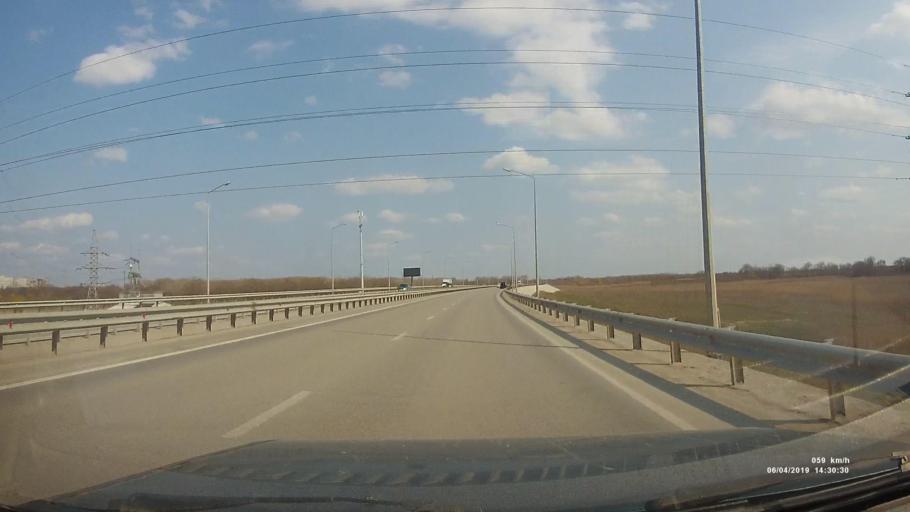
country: RU
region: Rostov
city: Rostov-na-Donu
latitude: 47.2070
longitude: 39.7482
